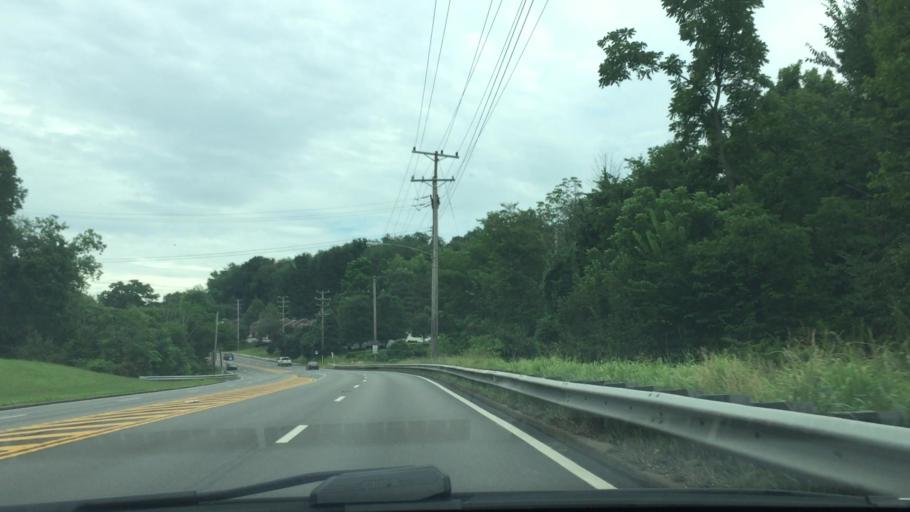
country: US
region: Pennsylvania
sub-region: Allegheny County
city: Mount Lebanon
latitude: 40.3597
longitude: -80.0612
